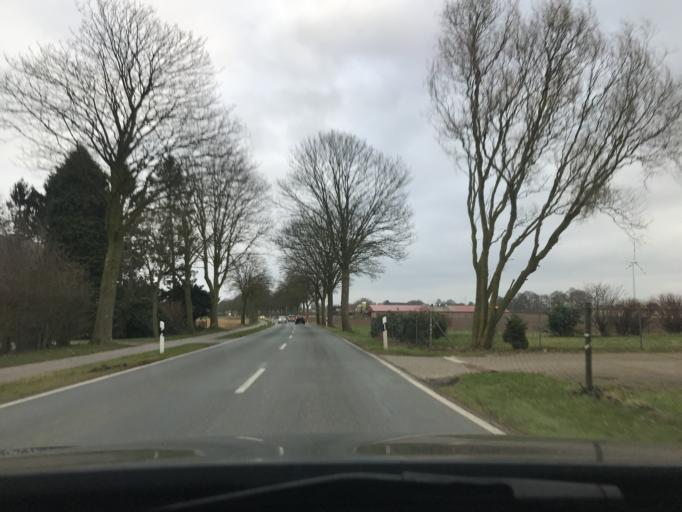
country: DE
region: North Rhine-Westphalia
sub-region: Regierungsbezirk Dusseldorf
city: Goch
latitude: 51.7350
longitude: 6.2019
